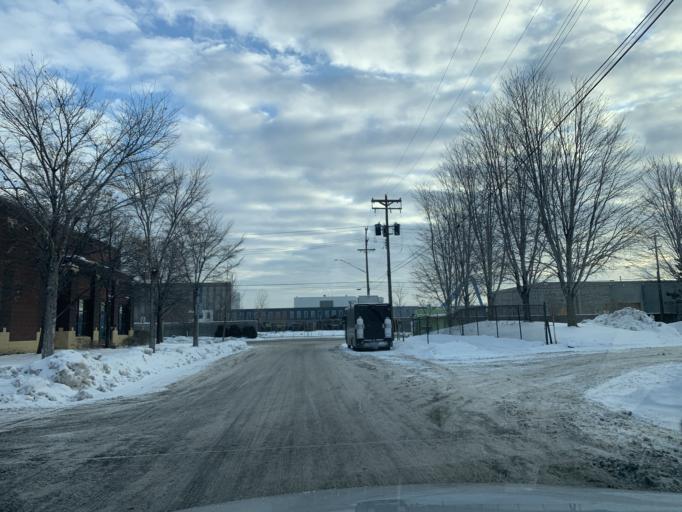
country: US
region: Minnesota
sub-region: Hennepin County
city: Minneapolis
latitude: 44.9953
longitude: -93.2807
